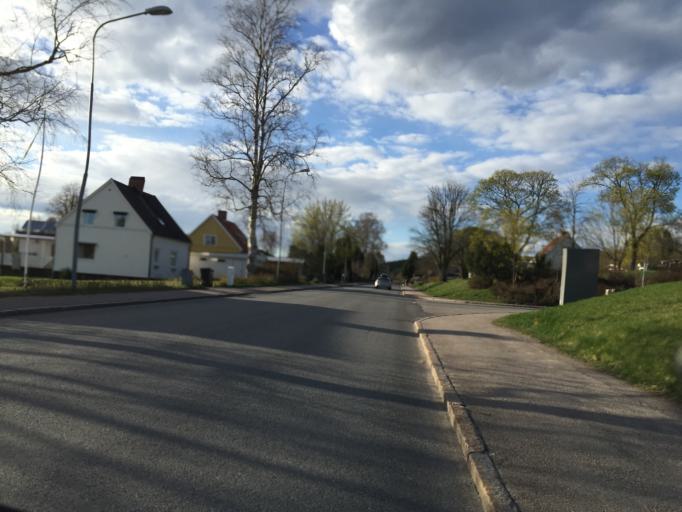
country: SE
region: Dalarna
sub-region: Ludvika Kommun
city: Ludvika
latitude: 60.1204
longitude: 15.1933
